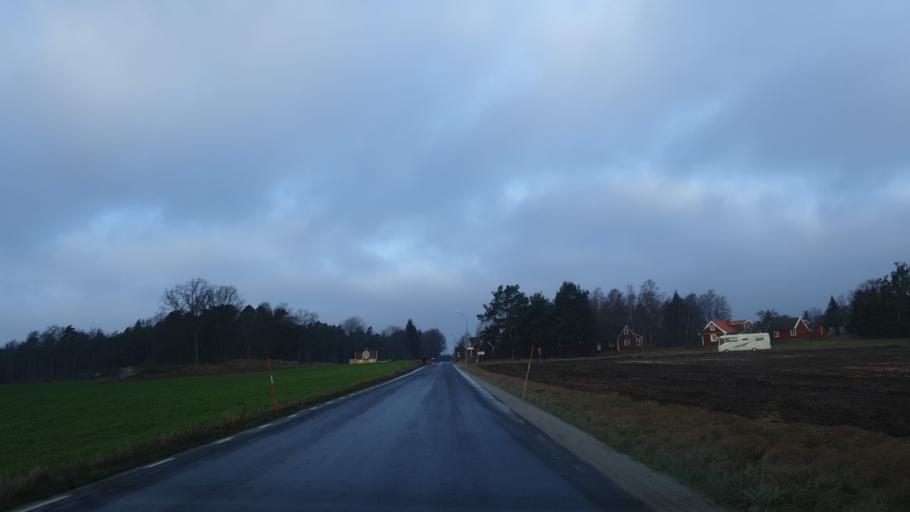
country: SE
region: Blekinge
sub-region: Karlshamns Kommun
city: Morrum
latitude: 56.1698
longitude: 14.7429
